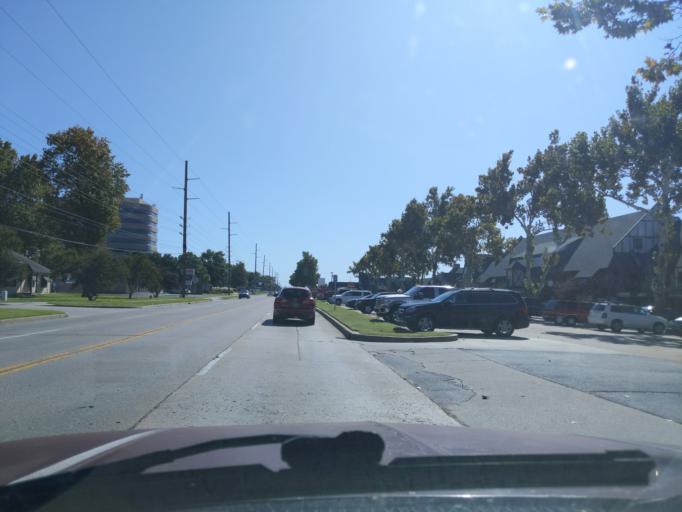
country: US
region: Oklahoma
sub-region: Tulsa County
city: Jenks
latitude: 36.0810
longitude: -95.9580
